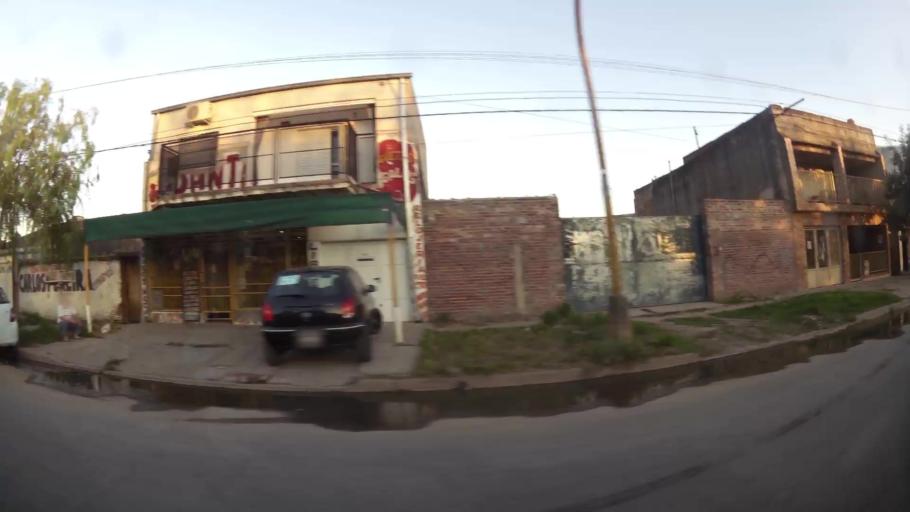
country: AR
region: Santa Fe
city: Santa Fe de la Vera Cruz
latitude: -31.5987
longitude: -60.7009
